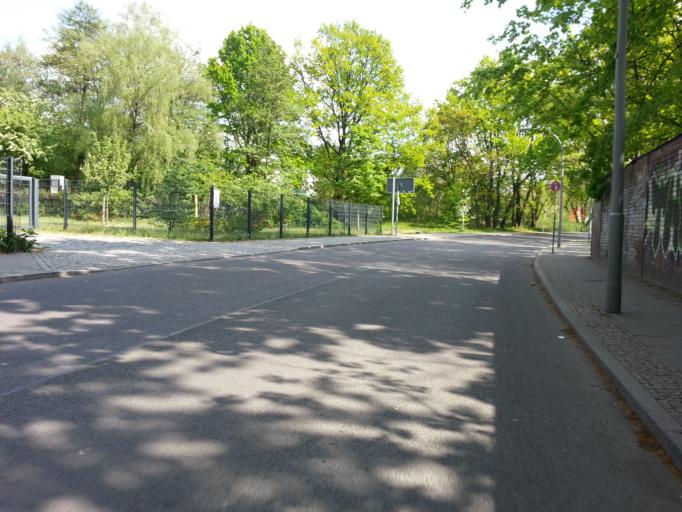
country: DE
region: Berlin
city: Haselhorst
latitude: 52.5418
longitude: 13.2305
